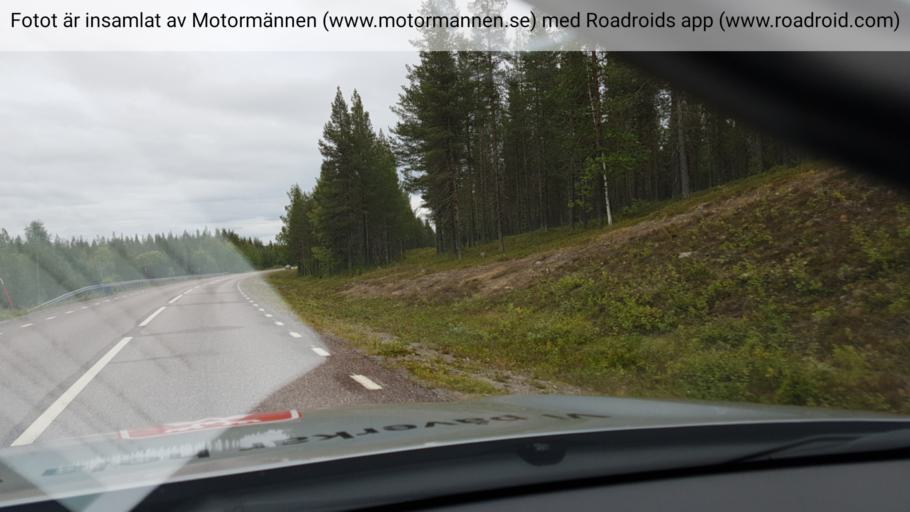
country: SE
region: Norrbotten
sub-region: Gallivare Kommun
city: Gaellivare
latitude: 67.0694
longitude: 21.5534
